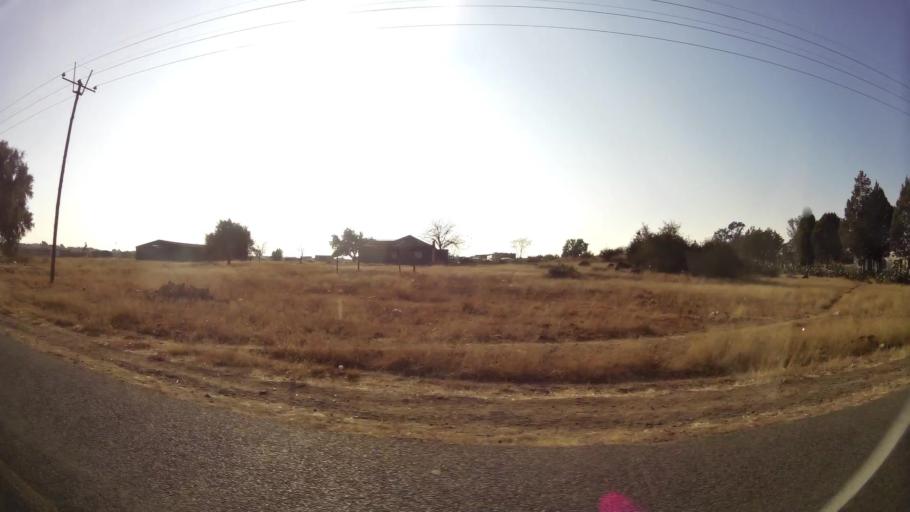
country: ZA
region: Orange Free State
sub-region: Mangaung Metropolitan Municipality
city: Bloemfontein
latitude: -29.1879
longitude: 26.2706
